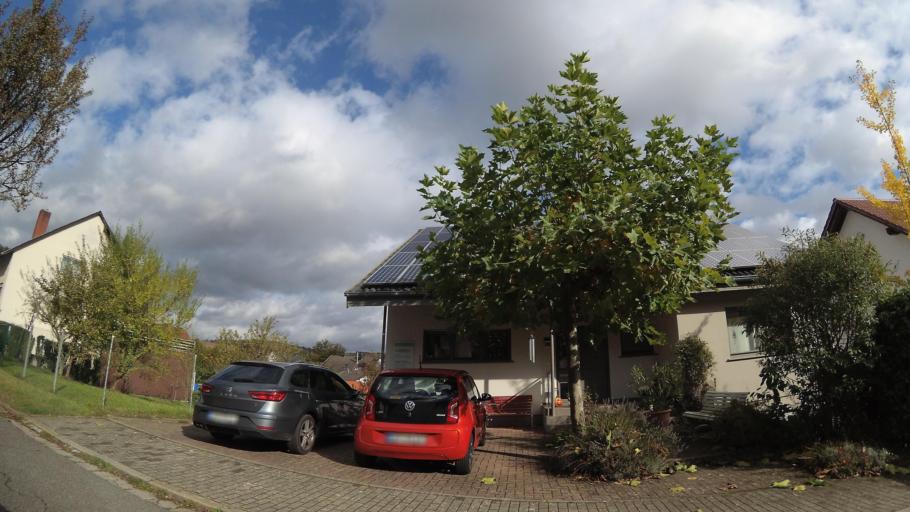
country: DE
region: Saarland
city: Blieskastel
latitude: 49.2561
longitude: 7.2466
